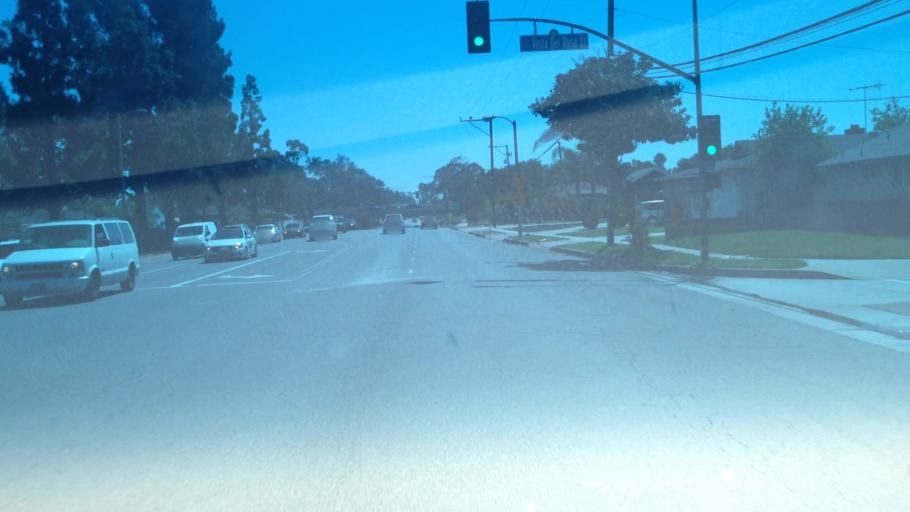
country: US
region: California
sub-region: Los Angeles County
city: Pico Rivera
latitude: 33.9660
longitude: -118.1176
